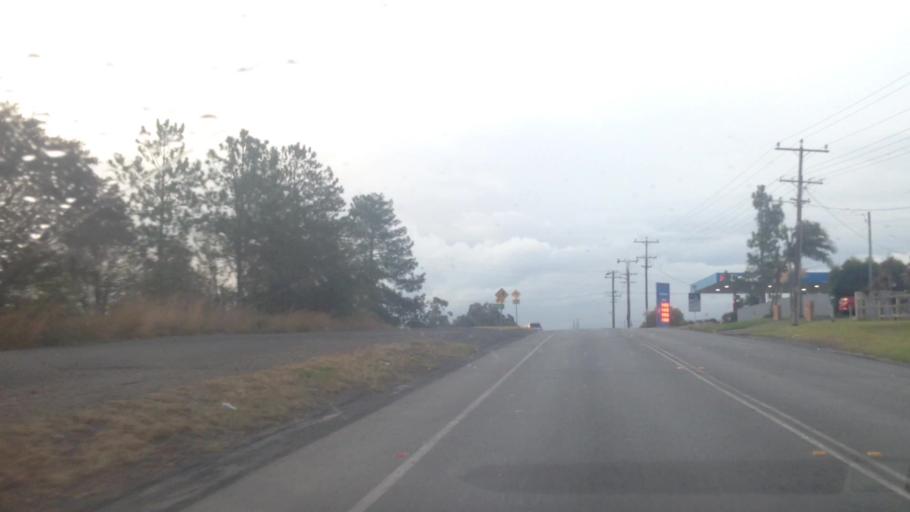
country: AU
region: New South Wales
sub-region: Wyong Shire
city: Charmhaven
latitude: -33.1770
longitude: 151.4873
